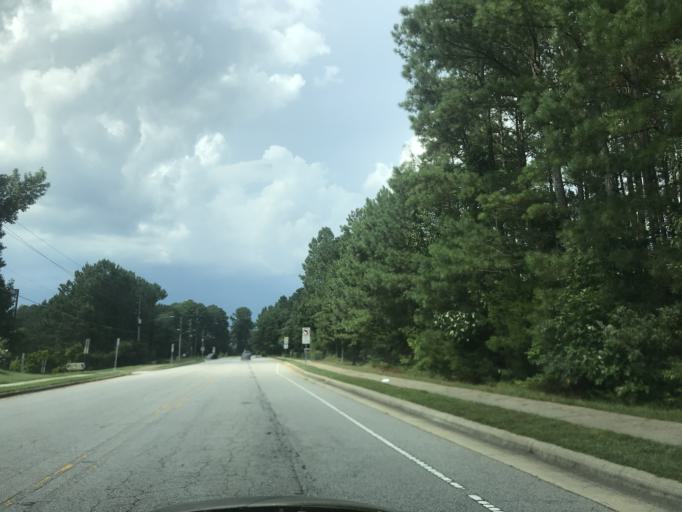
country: US
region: North Carolina
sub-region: Wake County
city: West Raleigh
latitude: 35.8898
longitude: -78.6558
